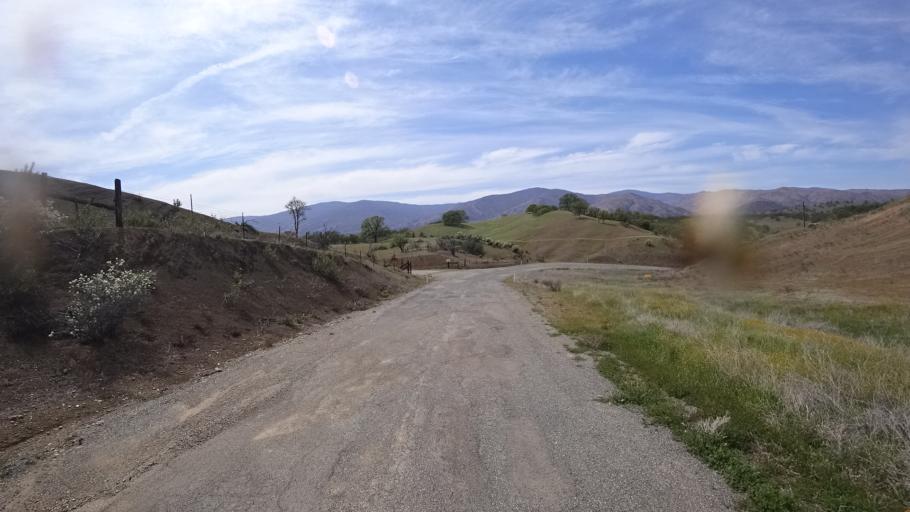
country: US
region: California
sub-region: Glenn County
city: Willows
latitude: 39.6058
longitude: -122.5574
